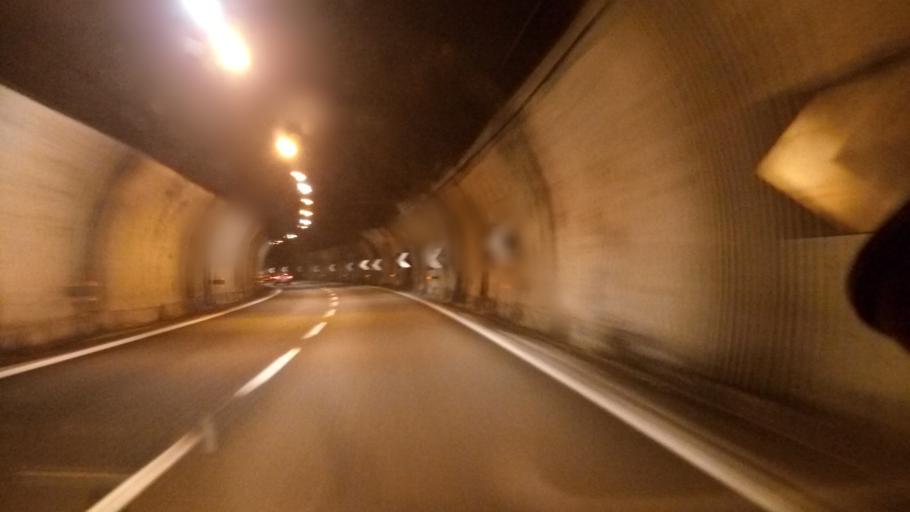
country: IT
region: Liguria
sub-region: Provincia di Genova
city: San Teodoro
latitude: 44.4306
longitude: 8.8512
